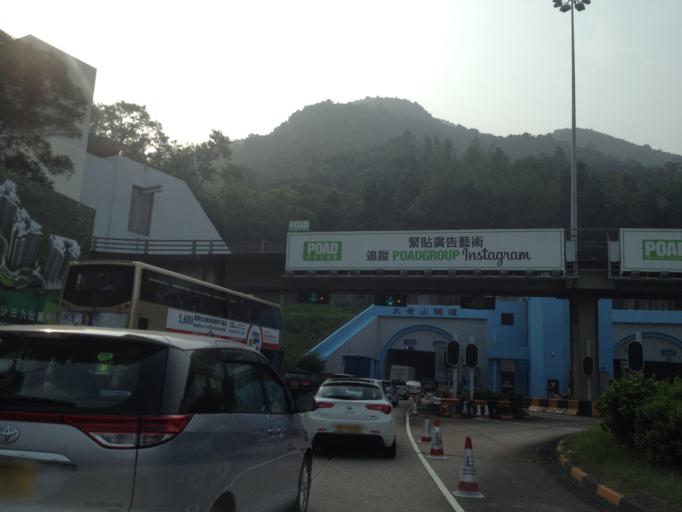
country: HK
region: Sha Tin
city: Sha Tin
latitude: 22.3767
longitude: 114.2127
